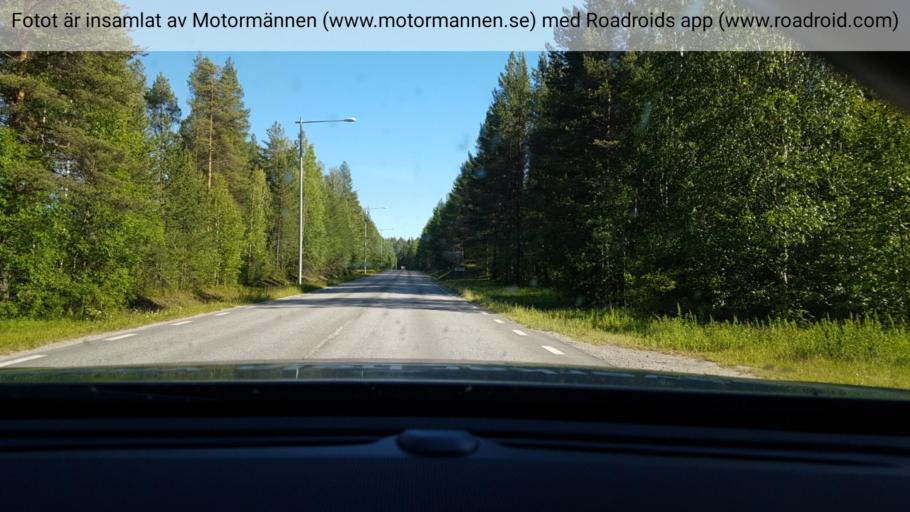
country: SE
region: Vaesterbotten
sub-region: Lycksele Kommun
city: Lycksele
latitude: 64.6135
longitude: 18.6423
